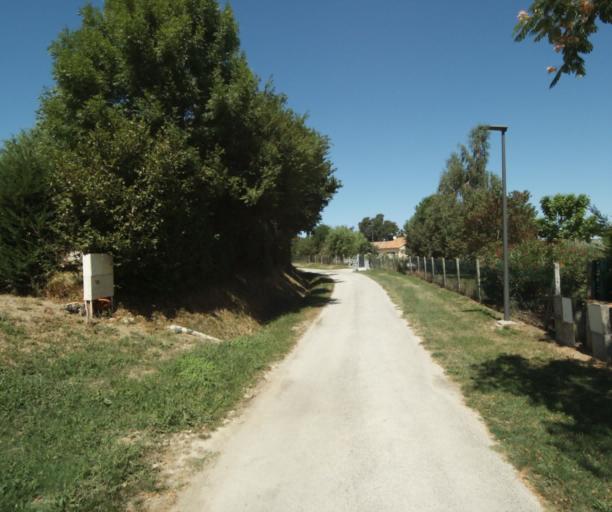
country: FR
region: Midi-Pyrenees
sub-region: Departement de la Haute-Garonne
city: Saint-Felix-Lauragais
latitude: 43.4648
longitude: 1.9277
